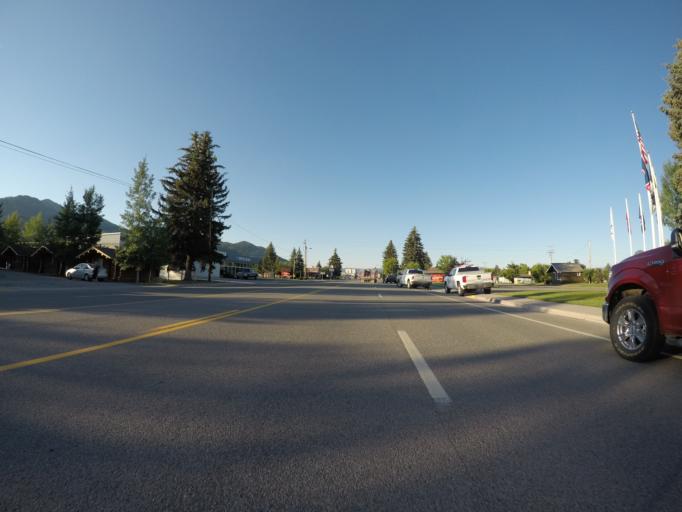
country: US
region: Wyoming
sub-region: Lincoln County
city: Afton
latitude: 42.7303
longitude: -110.9334
